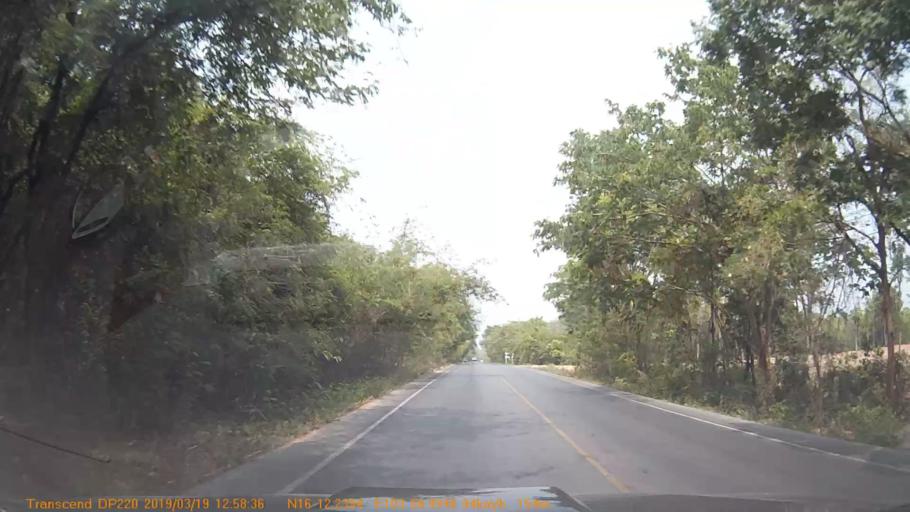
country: TH
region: Roi Et
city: Waeng
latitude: 16.2042
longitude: 103.9500
